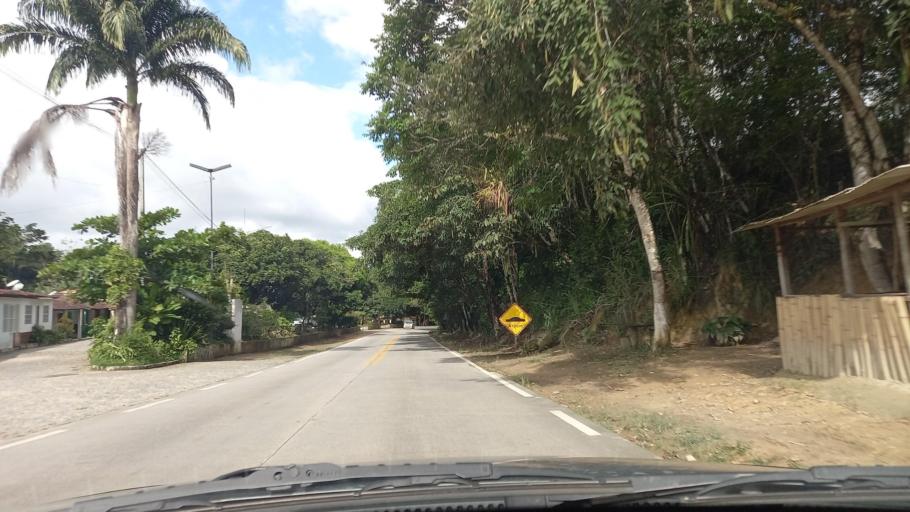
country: BR
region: Pernambuco
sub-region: Maraial
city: Maraial
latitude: -8.7902
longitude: -35.8929
